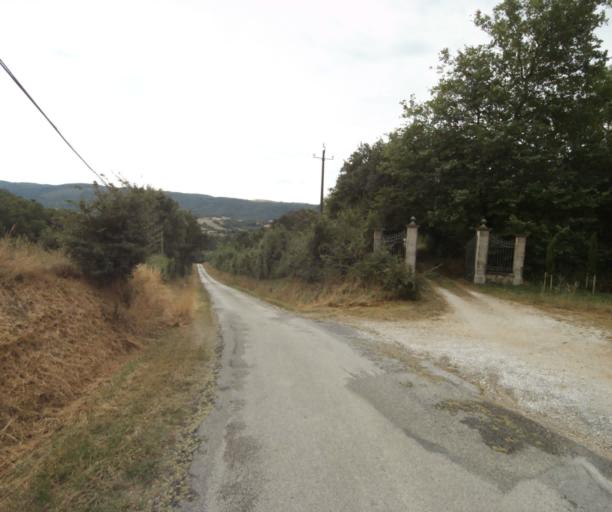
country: FR
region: Midi-Pyrenees
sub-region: Departement de la Haute-Garonne
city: Revel
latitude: 43.4308
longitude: 1.9767
